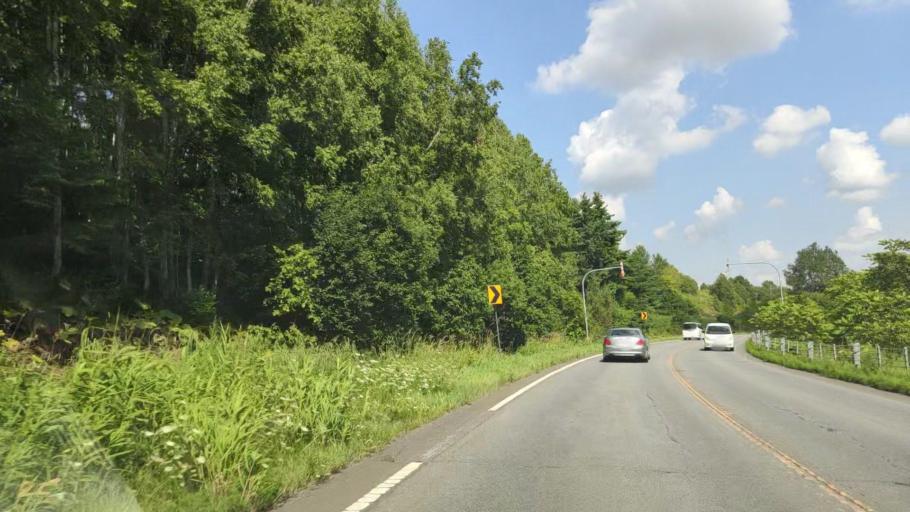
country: JP
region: Hokkaido
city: Shimo-furano
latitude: 43.5567
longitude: 142.4348
